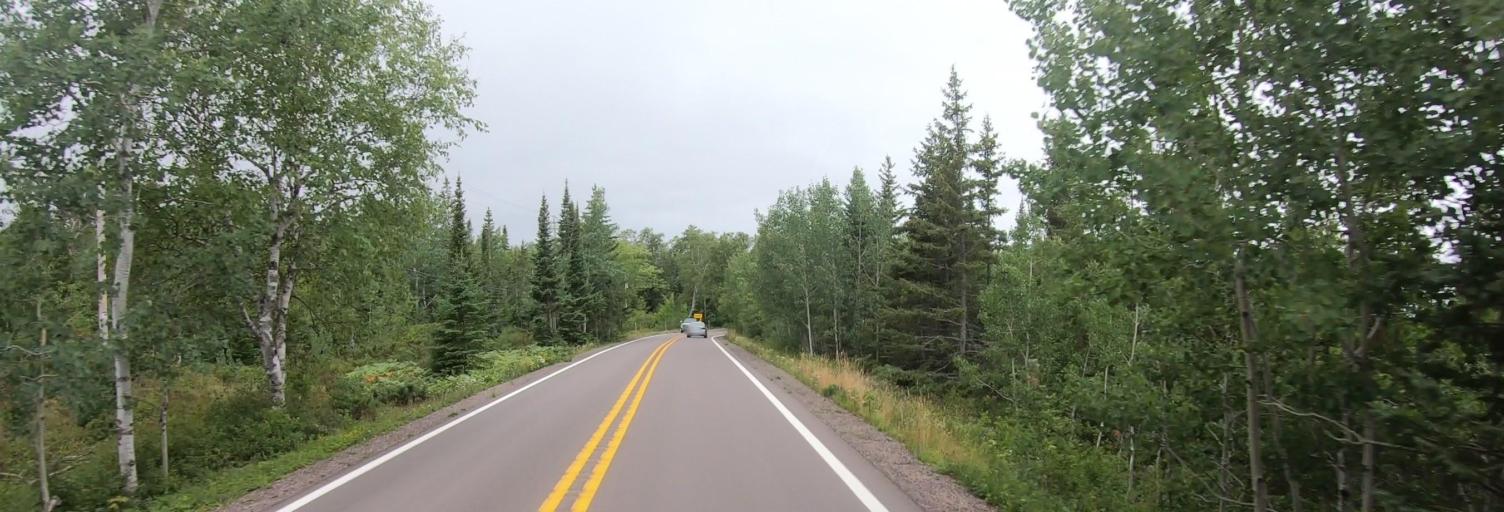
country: US
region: Michigan
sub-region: Keweenaw County
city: Eagle River
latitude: 47.4770
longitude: -88.0075
